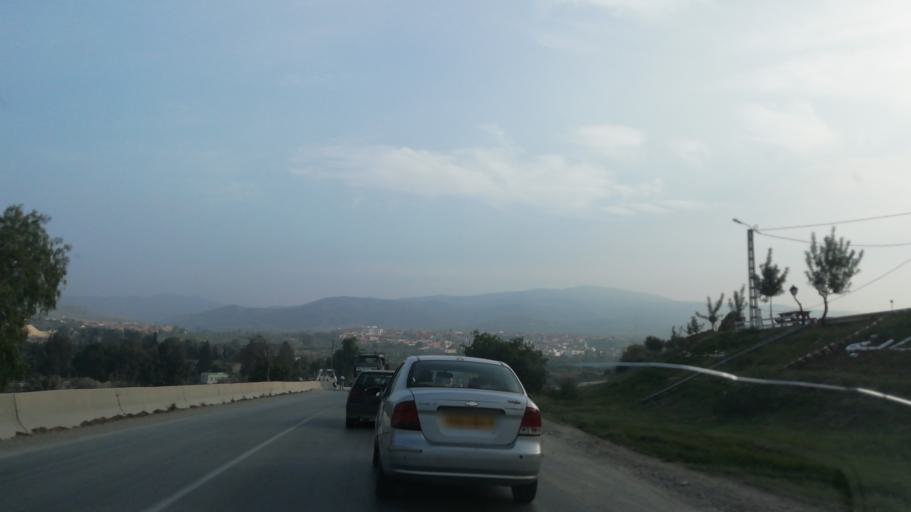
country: DZ
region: Mascara
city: Bou Hanifia el Hamamat
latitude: 35.4703
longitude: -0.0117
